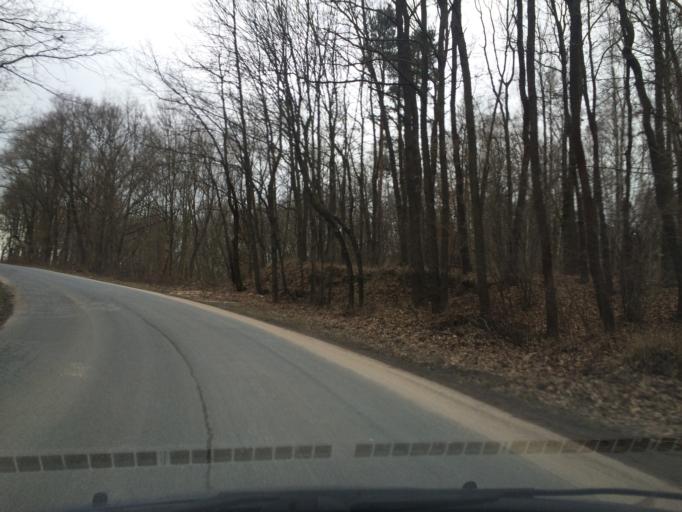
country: PL
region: Lower Silesian Voivodeship
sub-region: Powiat lwowecki
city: Lwowek Slaski
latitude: 51.1214
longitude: 15.5152
